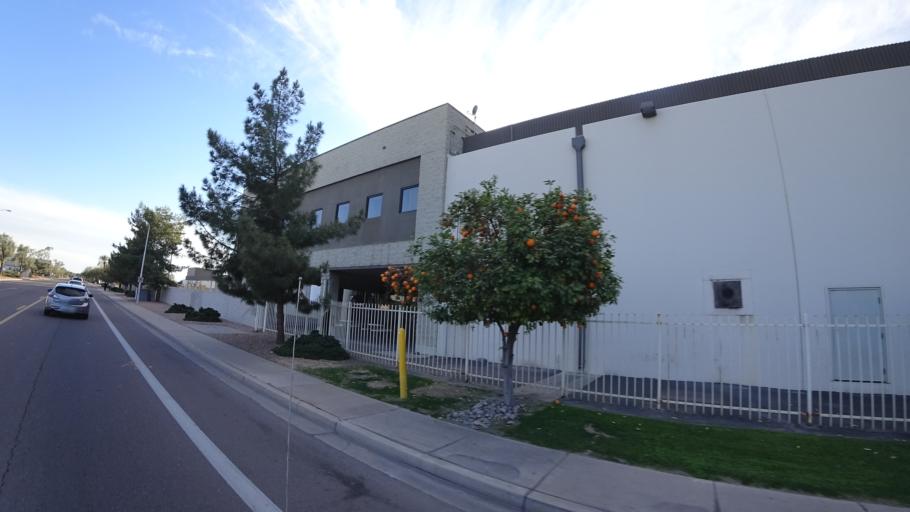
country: US
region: Arizona
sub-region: Maricopa County
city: Tempe Junction
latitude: 33.4052
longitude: -111.9522
